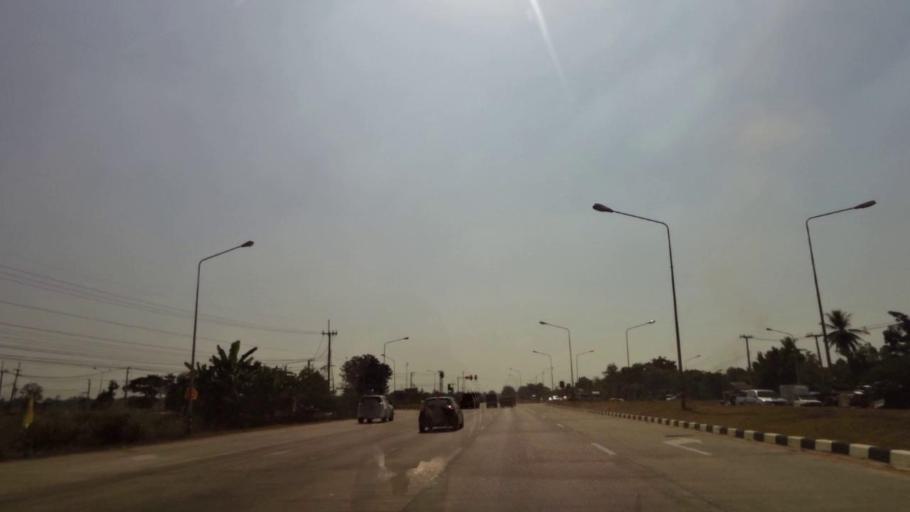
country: TH
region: Phichit
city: Wachira Barami
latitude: 16.3559
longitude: 100.1293
